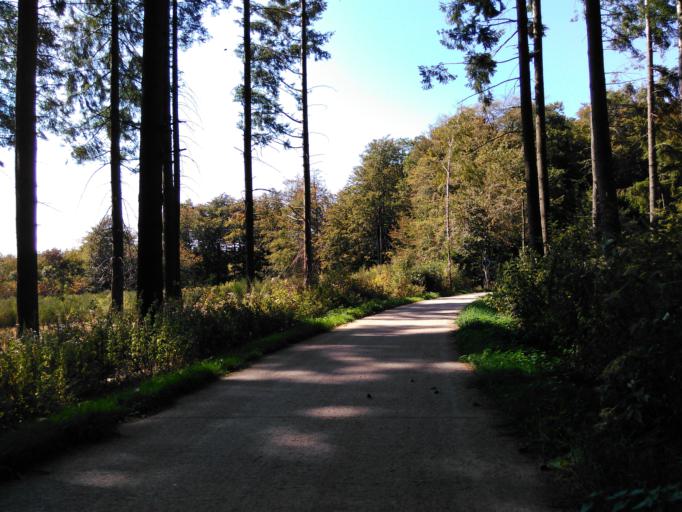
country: LU
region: Diekirch
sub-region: Canton de Redange
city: Rambrouch
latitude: 49.8369
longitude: 5.8249
